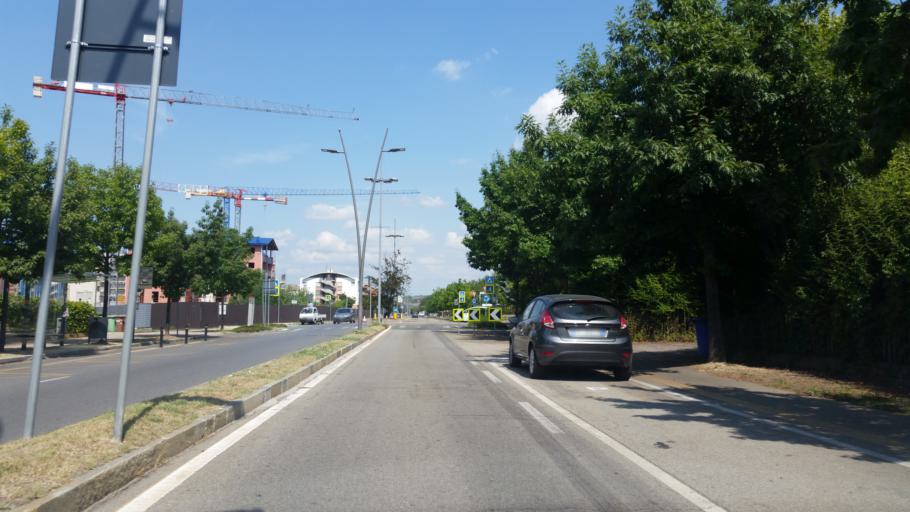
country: IT
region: Piedmont
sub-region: Provincia di Cuneo
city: Alba
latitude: 44.6903
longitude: 8.0160
